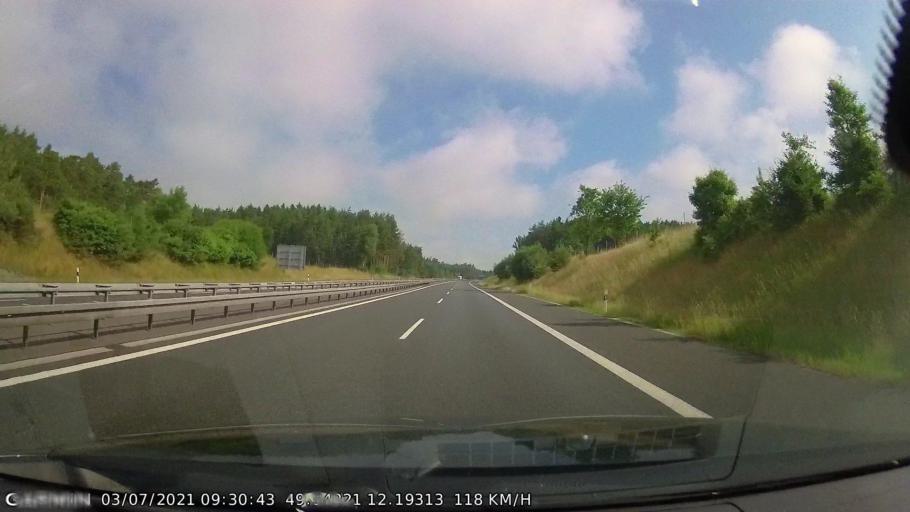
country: DE
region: Bavaria
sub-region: Upper Palatinate
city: Wernberg-Koblitz
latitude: 49.5423
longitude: 12.1932
